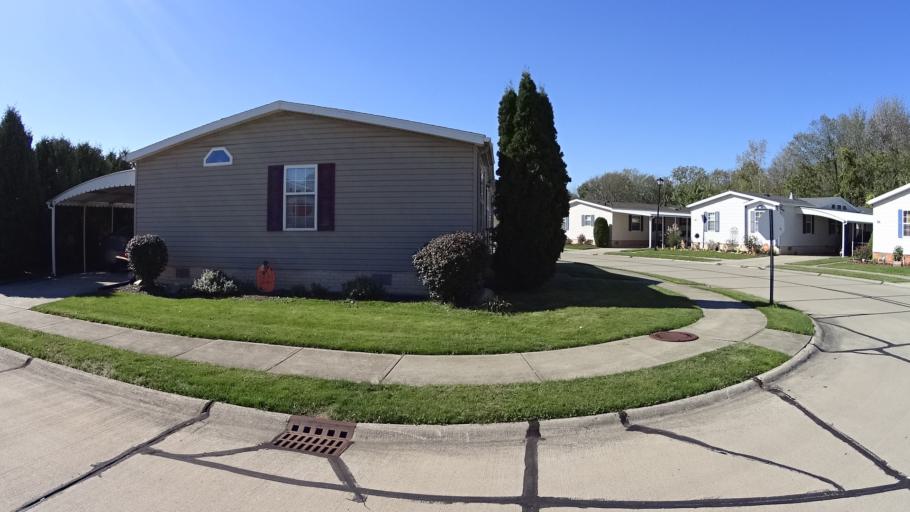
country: US
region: Ohio
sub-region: Lorain County
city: Amherst
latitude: 41.4113
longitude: -82.2022
